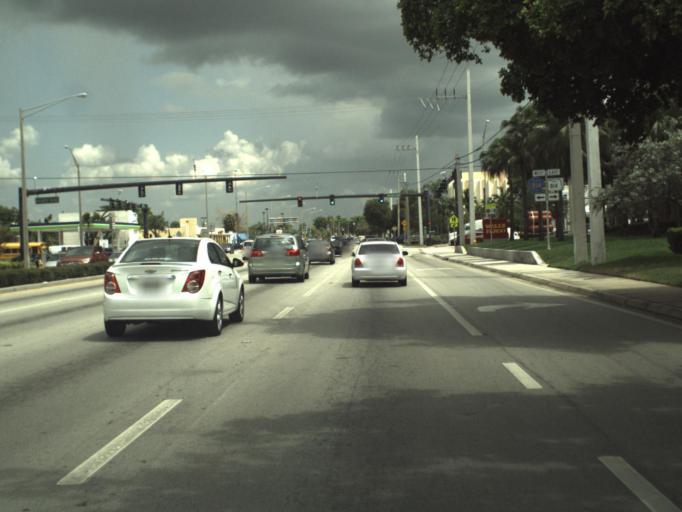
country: US
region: Florida
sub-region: Broward County
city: Margate
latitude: 26.2344
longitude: -80.2046
